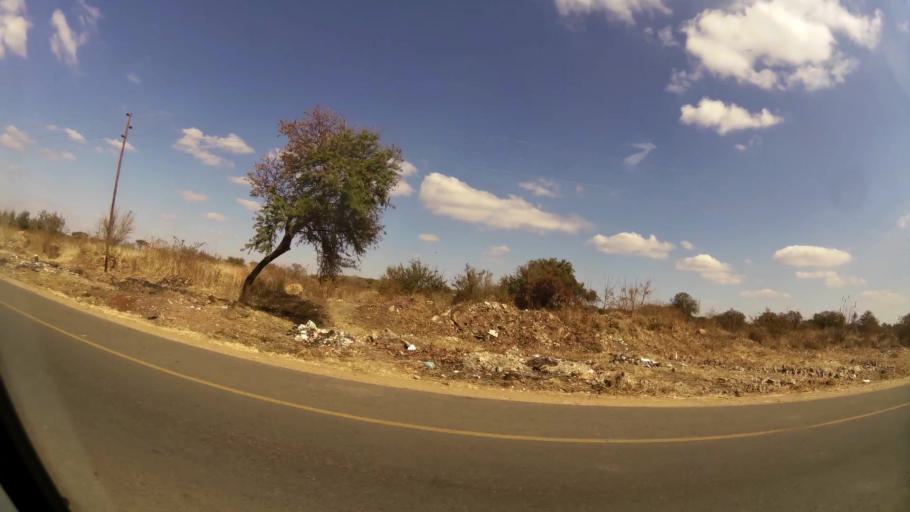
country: ZA
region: Gauteng
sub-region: City of Tshwane Metropolitan Municipality
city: Pretoria
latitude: -25.7456
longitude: 28.3525
